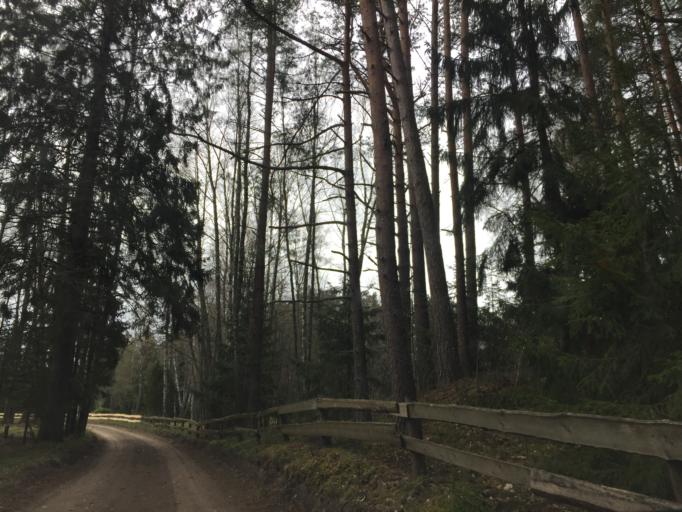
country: LV
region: Salacgrivas
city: Salacgriva
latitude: 57.5401
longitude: 24.3675
